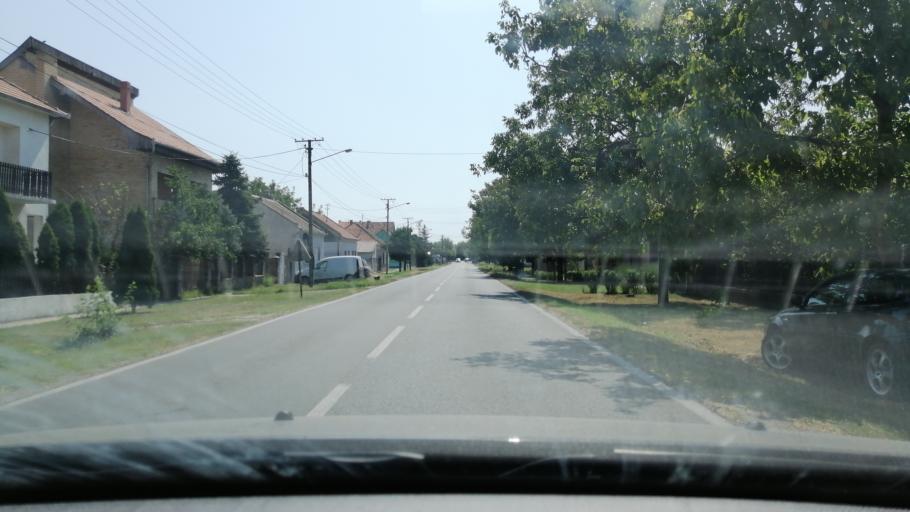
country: RS
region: Autonomna Pokrajina Vojvodina
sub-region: Juznobanatski Okrug
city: Pancevo
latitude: 44.8016
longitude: 20.7158
